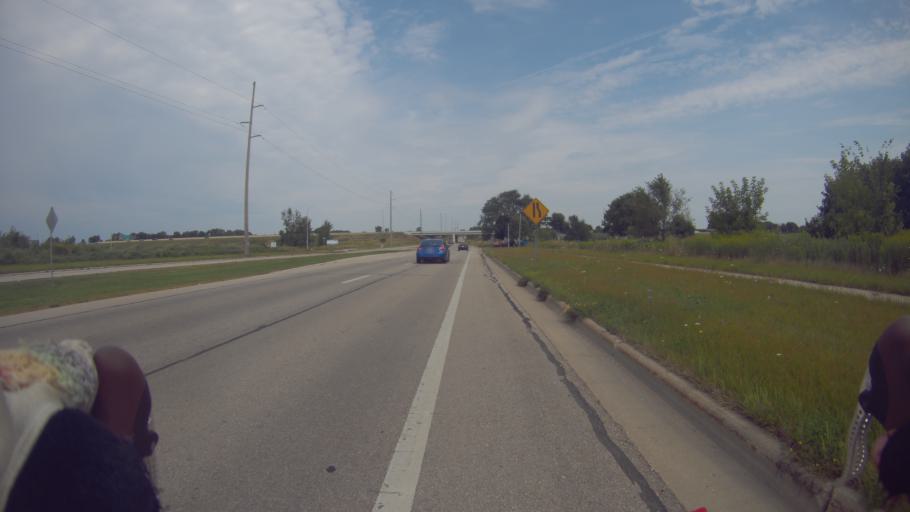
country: US
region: Wisconsin
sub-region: Dane County
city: Cottage Grove
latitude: 43.1007
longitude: -89.2666
